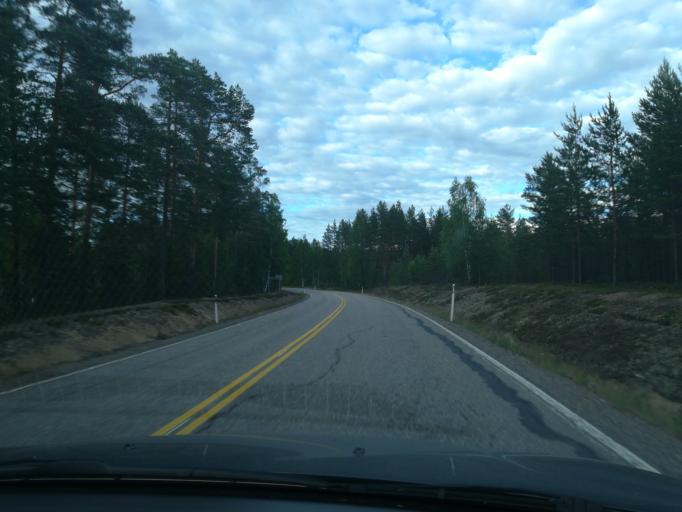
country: FI
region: Southern Savonia
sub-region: Mikkeli
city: Puumala
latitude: 61.5603
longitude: 28.0340
